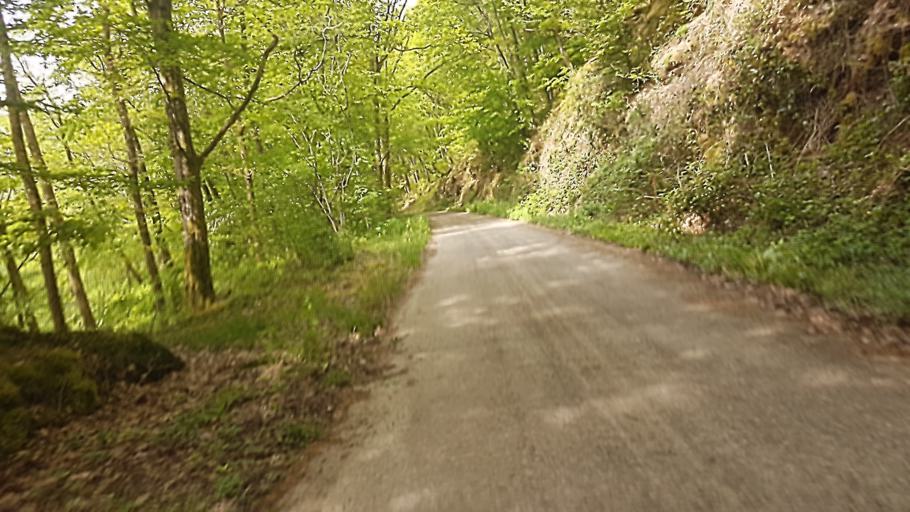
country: BE
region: Wallonia
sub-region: Province de Namur
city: Couvin
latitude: 50.0486
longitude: 4.5941
